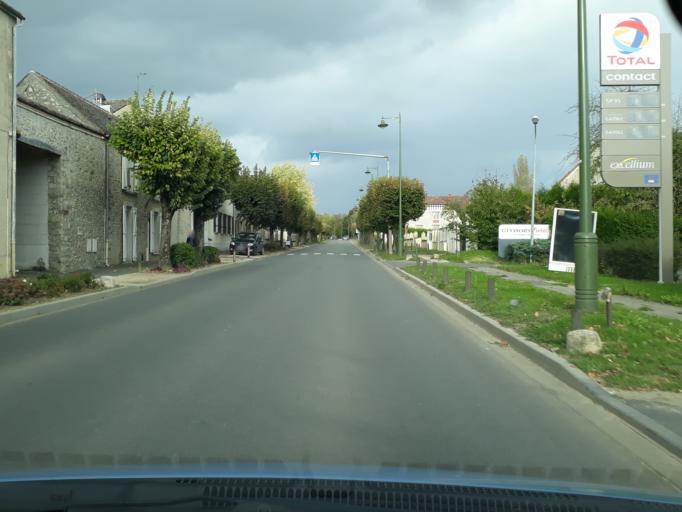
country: FR
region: Ile-de-France
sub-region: Departement de Seine-et-Marne
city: La Chapelle-la-Reine
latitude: 48.3192
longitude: 2.5740
